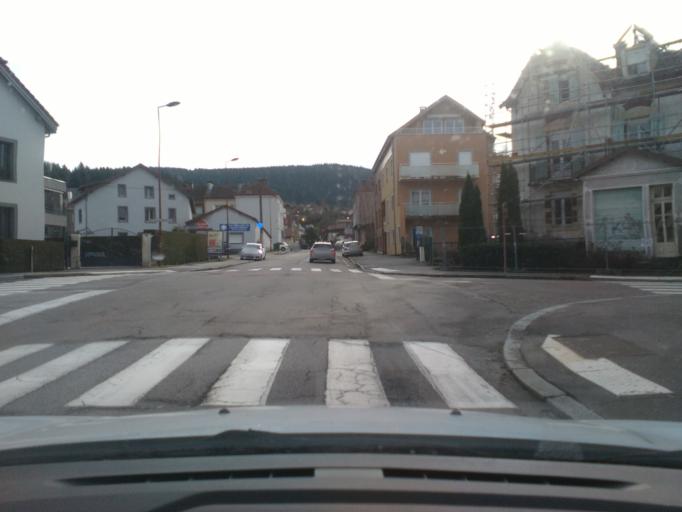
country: FR
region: Lorraine
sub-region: Departement des Vosges
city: Gerardmer
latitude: 48.0692
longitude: 6.8718
